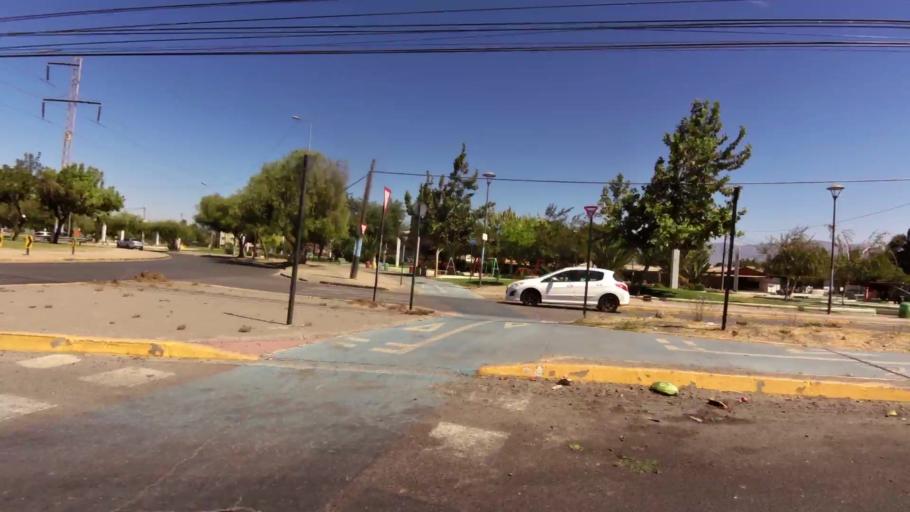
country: CL
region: O'Higgins
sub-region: Provincia de Cachapoal
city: Rancagua
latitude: -34.1681
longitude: -70.7177
